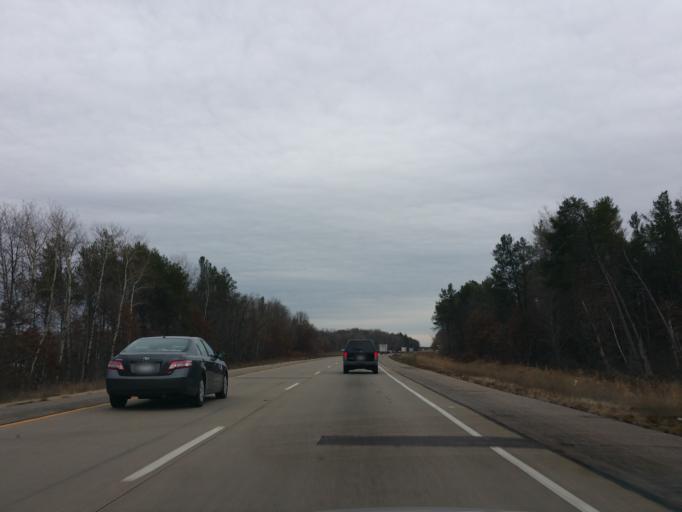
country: US
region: Wisconsin
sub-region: Juneau County
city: New Lisbon
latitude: 43.8720
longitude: -90.1274
